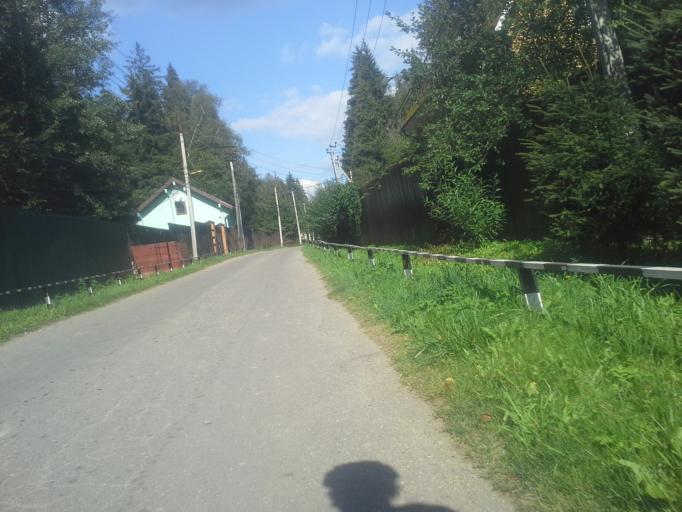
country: RU
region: Moskovskaya
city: Selyatino
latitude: 55.4666
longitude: 36.9934
